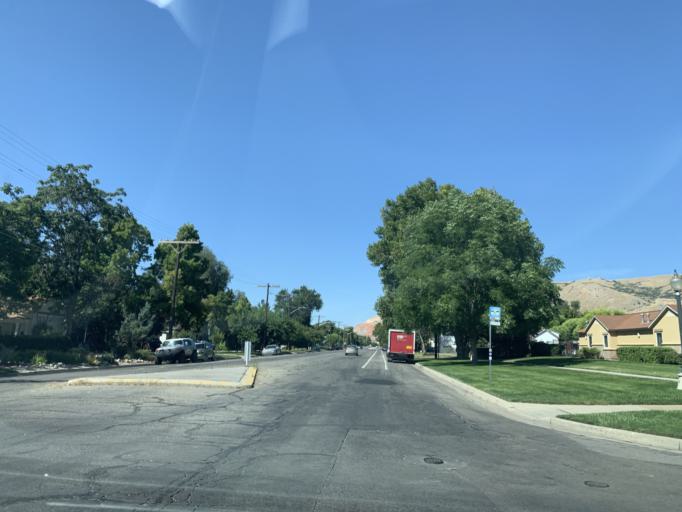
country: US
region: Utah
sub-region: Salt Lake County
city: Salt Lake City
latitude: 40.7738
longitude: -111.9082
